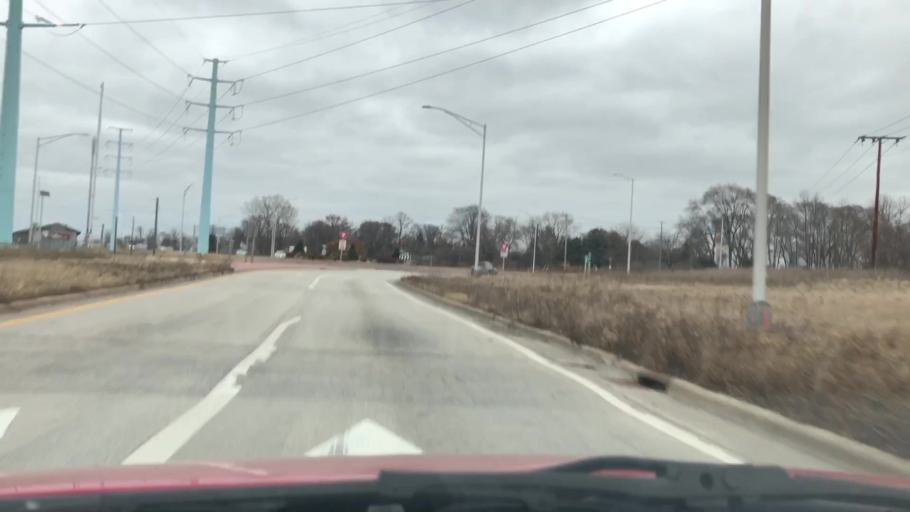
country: US
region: Wisconsin
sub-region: Brown County
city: De Pere
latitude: 44.4564
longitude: -88.0780
